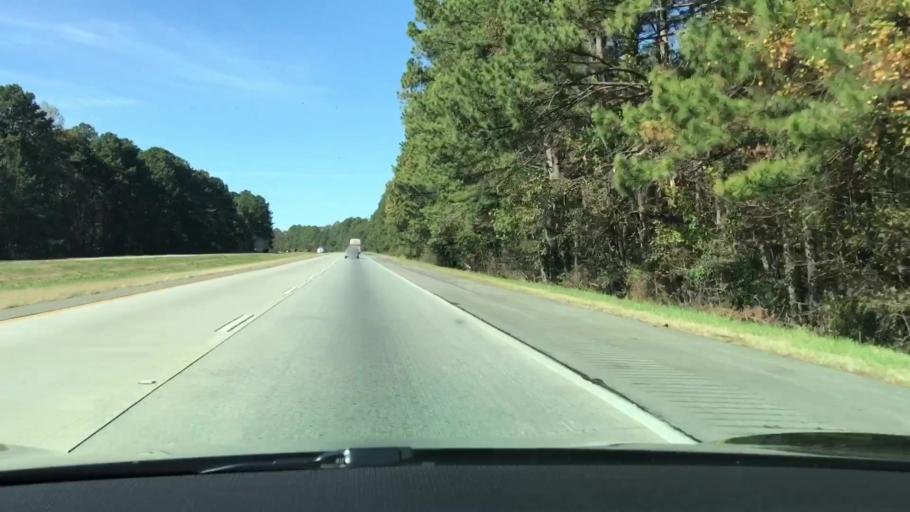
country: US
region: Georgia
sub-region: Greene County
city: Union Point
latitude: 33.5494
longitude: -83.0489
